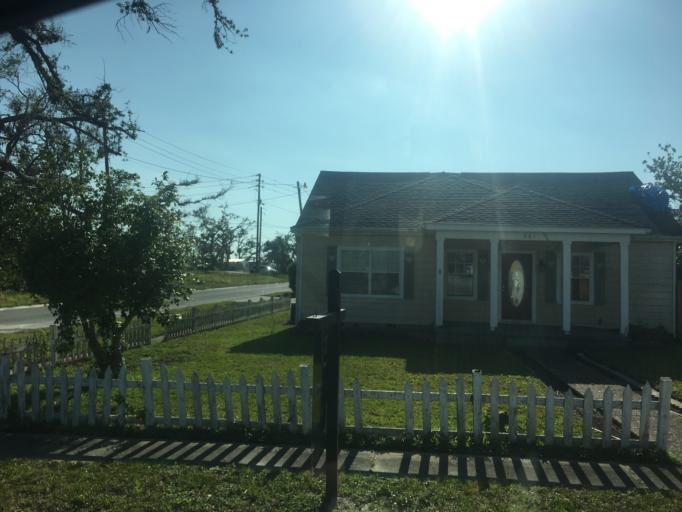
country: US
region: Florida
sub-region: Bay County
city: Panama City
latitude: 30.1587
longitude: -85.6410
